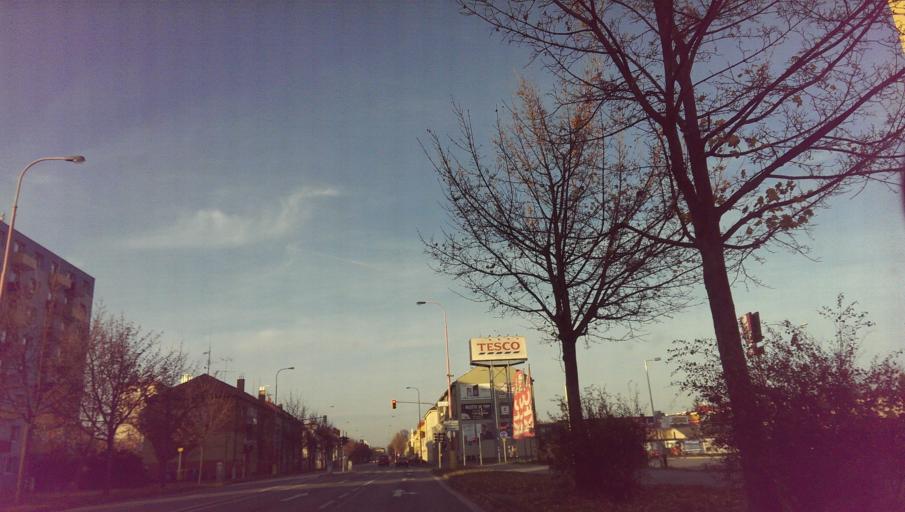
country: CZ
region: Zlin
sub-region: Okres Uherske Hradiste
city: Uherske Hradiste
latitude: 49.0612
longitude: 17.4666
